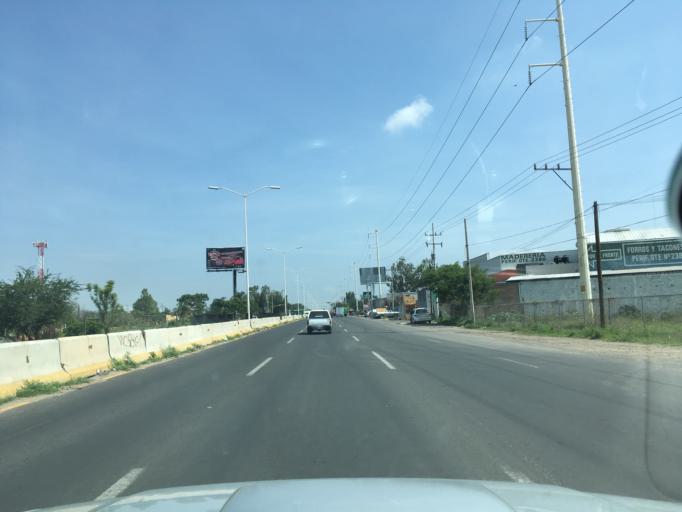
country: MX
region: Jalisco
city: Tonala
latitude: 20.6666
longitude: -103.2338
